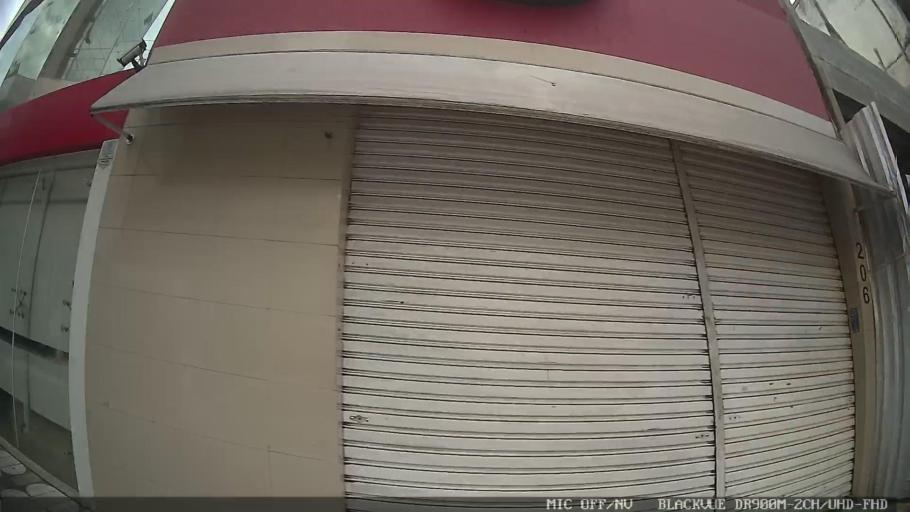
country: BR
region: Sao Paulo
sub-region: Mogi das Cruzes
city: Mogi das Cruzes
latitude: -23.5231
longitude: -46.1966
